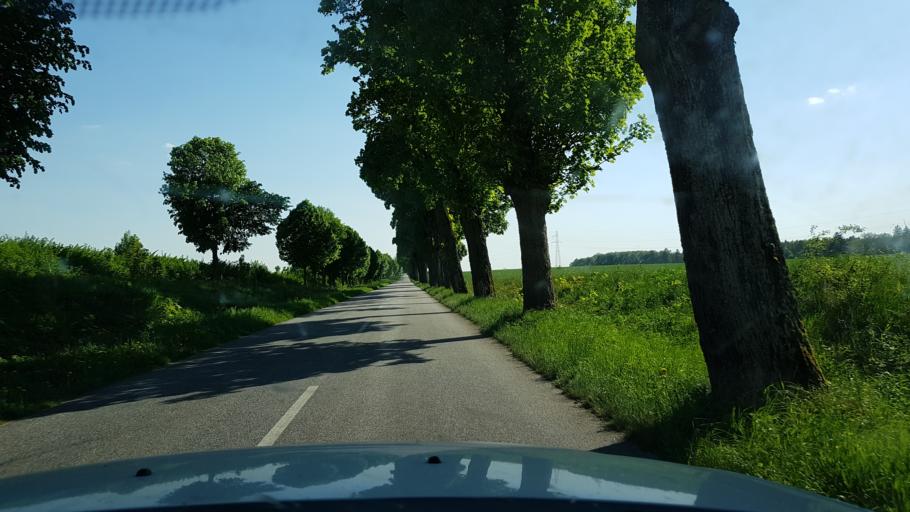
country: PL
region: West Pomeranian Voivodeship
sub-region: Powiat lobeski
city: Resko
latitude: 53.8044
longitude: 15.4181
